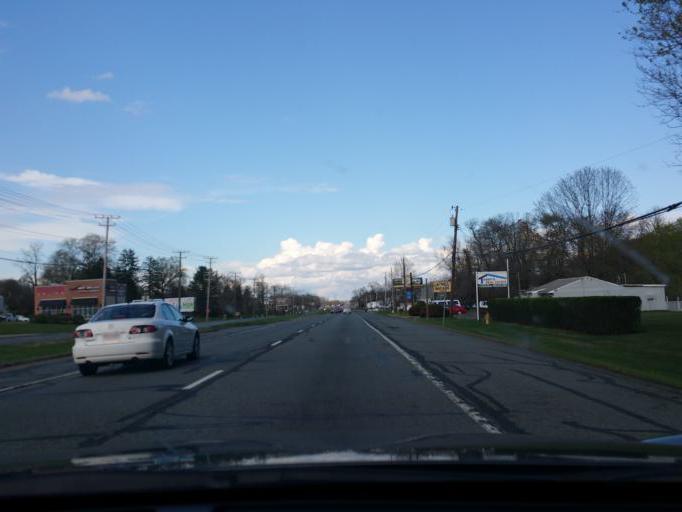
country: US
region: Maryland
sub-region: Harford County
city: Aberdeen
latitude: 39.5280
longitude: -76.1307
